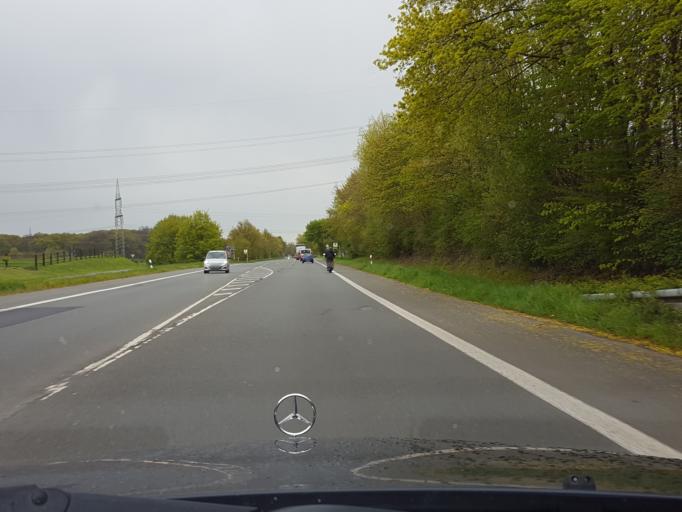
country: DE
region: North Rhine-Westphalia
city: Datteln
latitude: 51.6379
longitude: 7.3766
